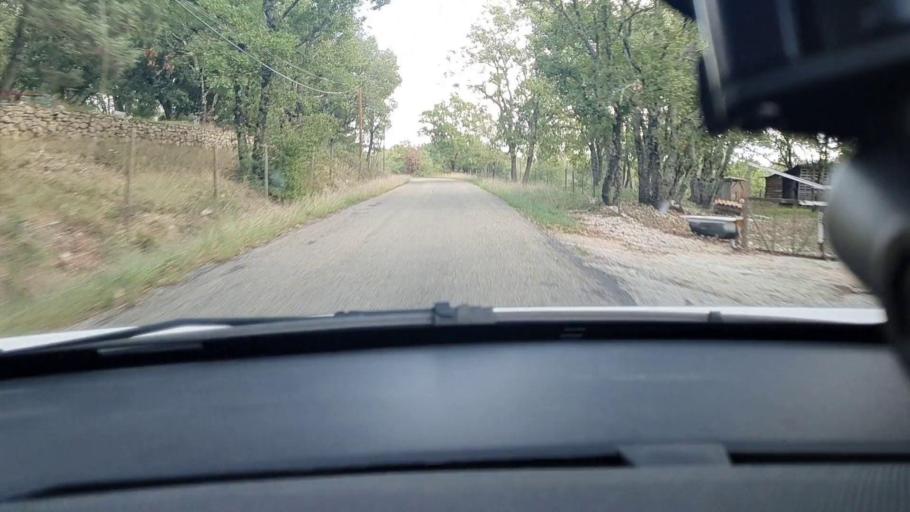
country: FR
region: Languedoc-Roussillon
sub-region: Departement du Gard
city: Mons
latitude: 44.1634
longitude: 4.3085
